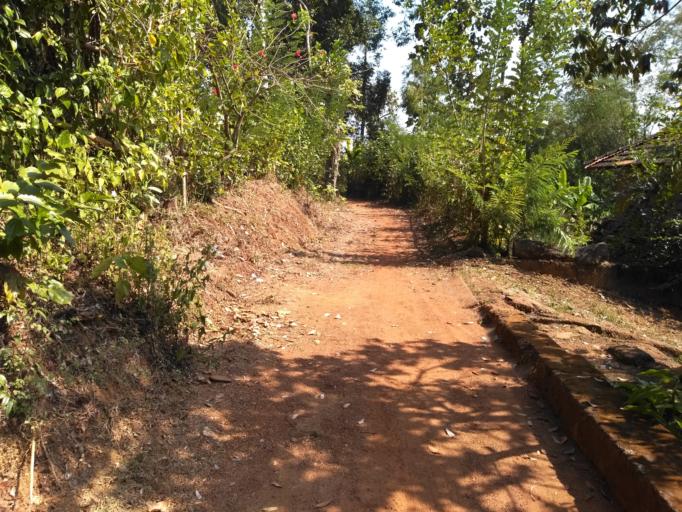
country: IN
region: Maharashtra
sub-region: Sindhudurg
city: Kudal
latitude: 16.0397
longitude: 73.6836
